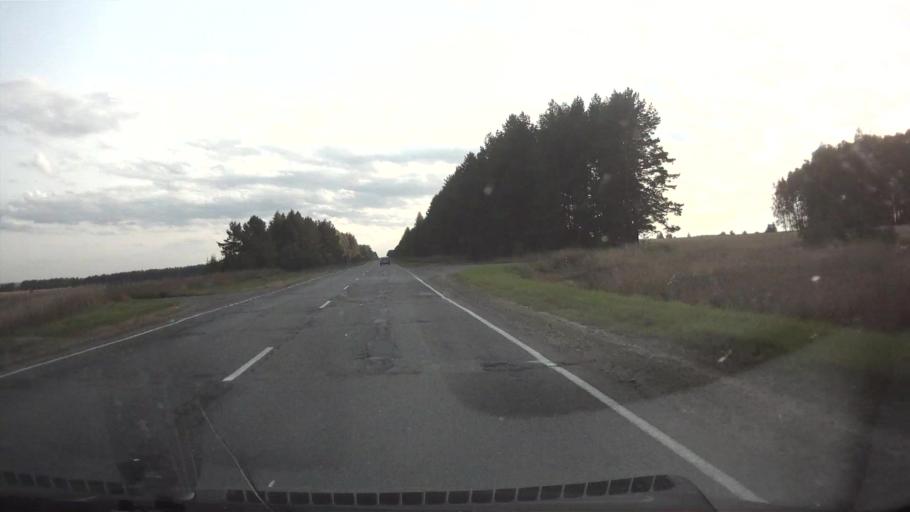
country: RU
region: Mariy-El
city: Kuzhener
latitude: 56.8394
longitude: 48.7364
